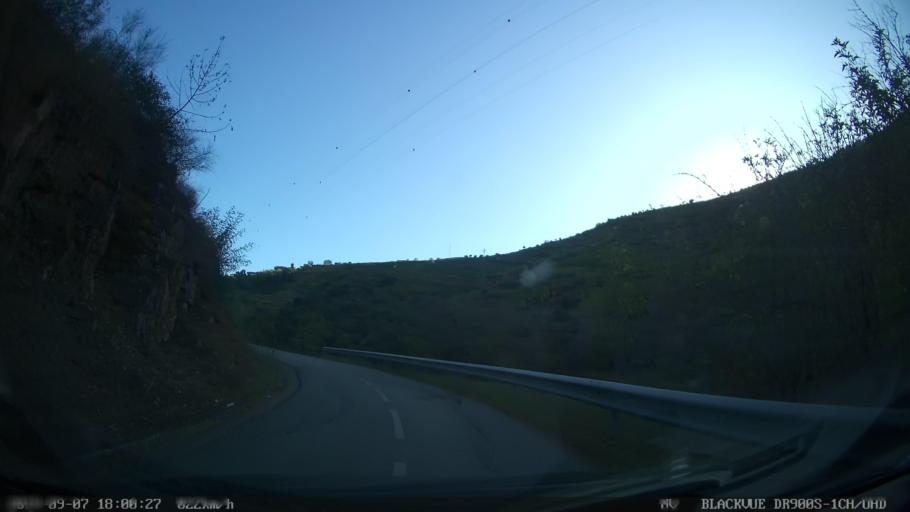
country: PT
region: Vila Real
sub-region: Peso da Regua
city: Peso da Regua
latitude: 41.1957
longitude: -7.7636
